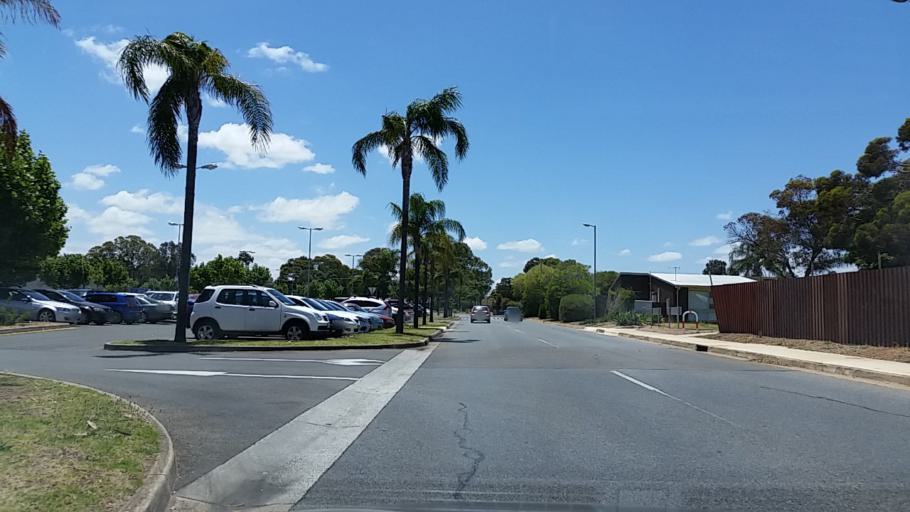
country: AU
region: South Australia
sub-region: Salisbury
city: Salisbury
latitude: -34.7684
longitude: 138.6259
